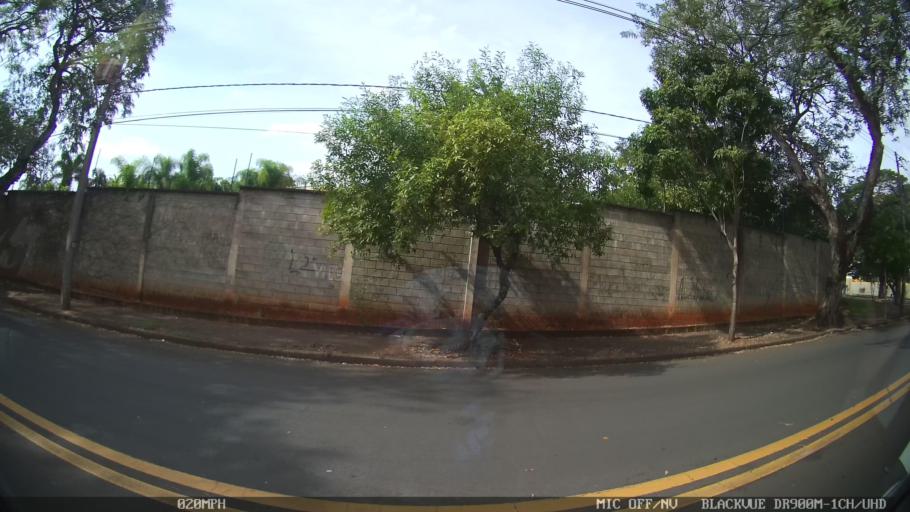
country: BR
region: Sao Paulo
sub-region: Piracicaba
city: Piracicaba
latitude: -22.7173
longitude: -47.6704
